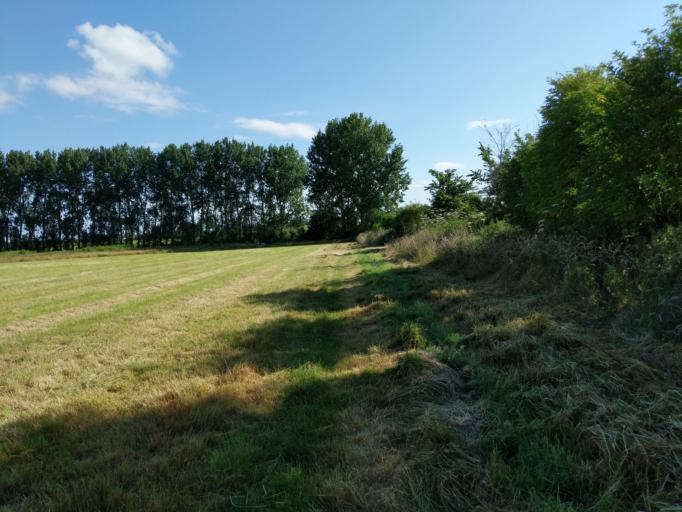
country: GB
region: England
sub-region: Kent
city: Faversham
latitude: 51.3280
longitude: 0.9376
